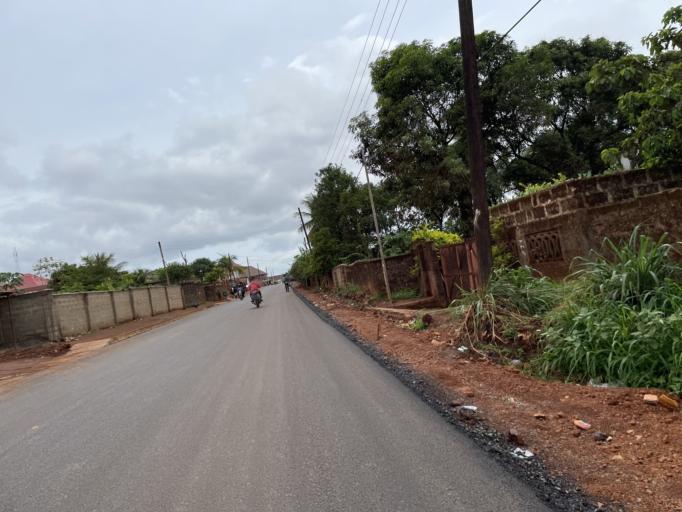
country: SL
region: Western Area
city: Hastings
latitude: 8.4060
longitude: -13.1437
